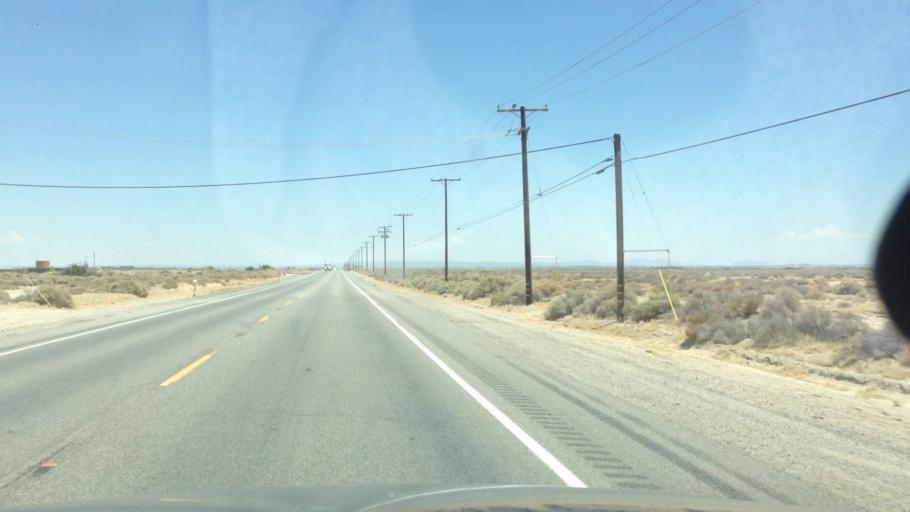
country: US
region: California
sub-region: Kern County
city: Rosamond
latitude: 34.7767
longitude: -118.1943
